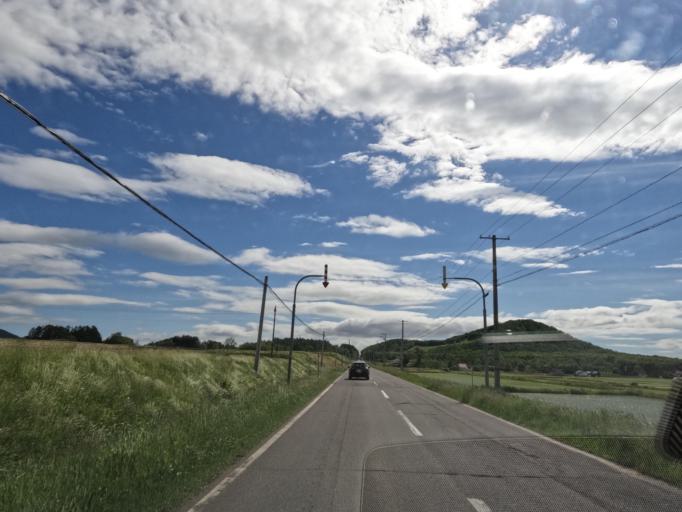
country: JP
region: Hokkaido
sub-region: Asahikawa-shi
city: Asahikawa
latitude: 43.8421
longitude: 142.5479
